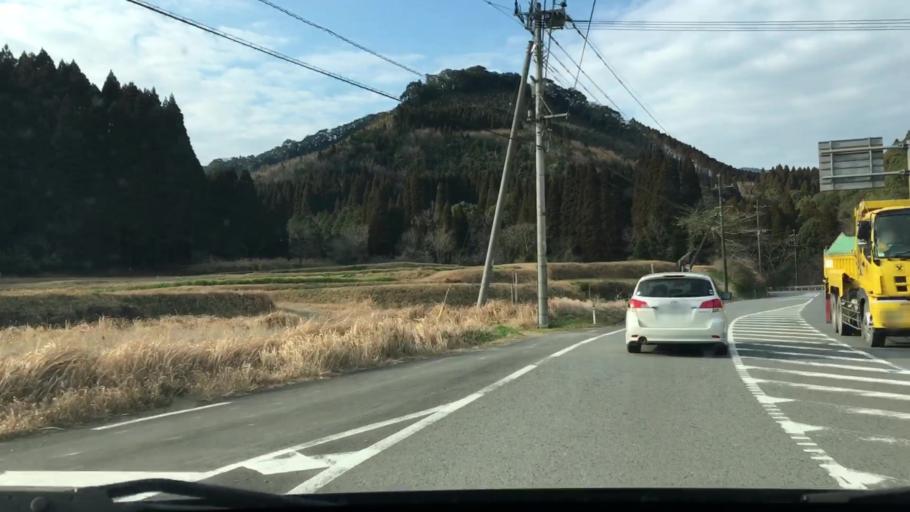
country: JP
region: Miyazaki
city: Nichinan
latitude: 31.7454
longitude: 131.3360
